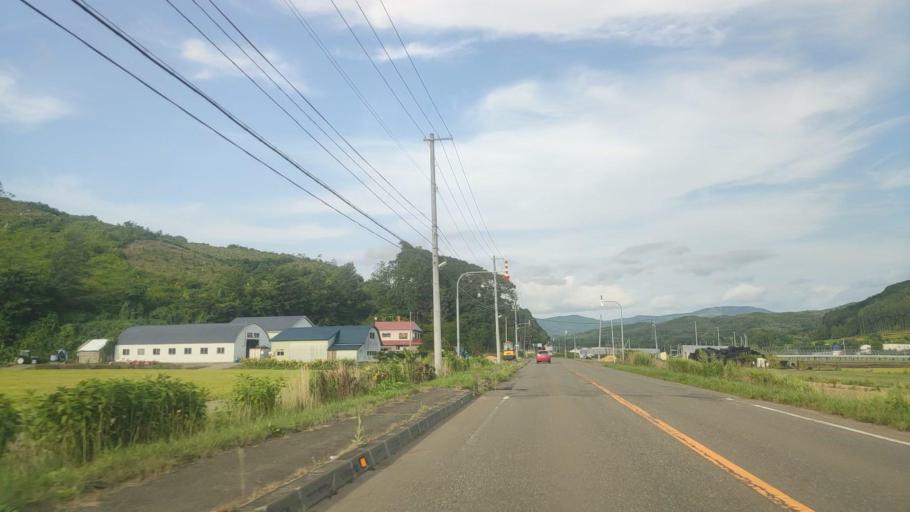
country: JP
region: Hokkaido
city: Iwamizawa
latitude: 43.0242
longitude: 141.8722
